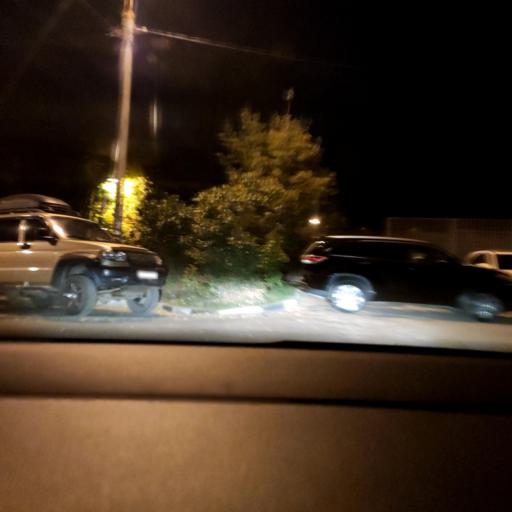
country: RU
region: Moskovskaya
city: Bolshevo
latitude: 55.9471
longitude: 37.8356
